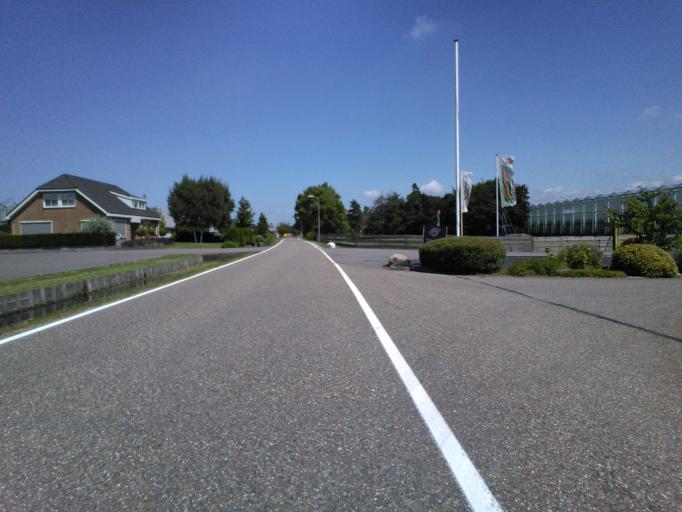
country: NL
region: South Holland
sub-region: Gemeente Westland
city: De Lier
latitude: 51.9626
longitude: 4.2341
